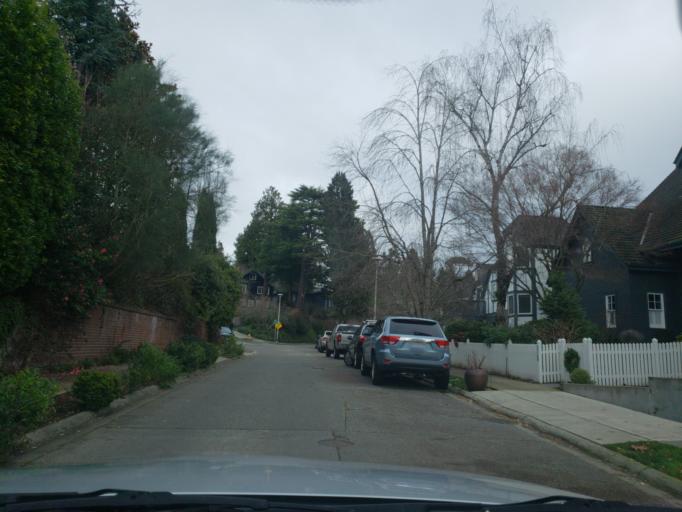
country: US
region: Washington
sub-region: King County
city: Medina
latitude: 47.6529
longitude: -122.2773
